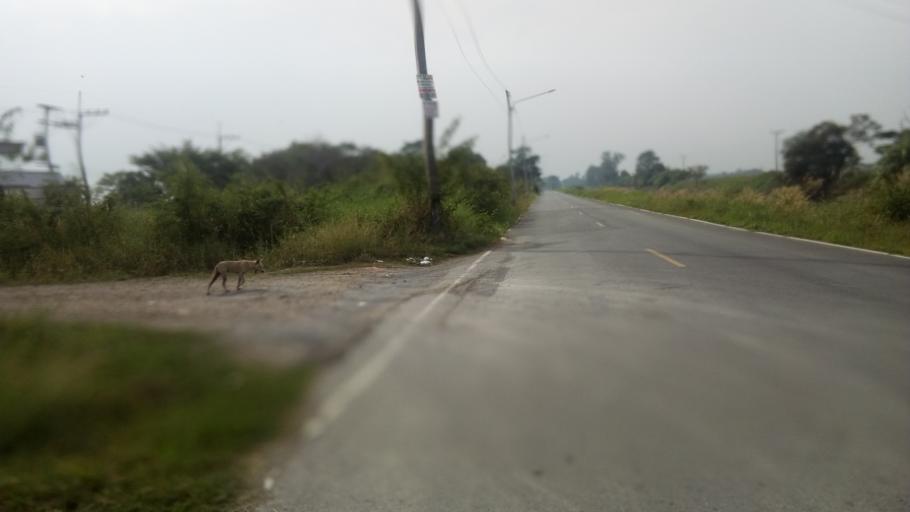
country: TH
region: Pathum Thani
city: Nong Suea
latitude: 14.0526
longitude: 100.8466
